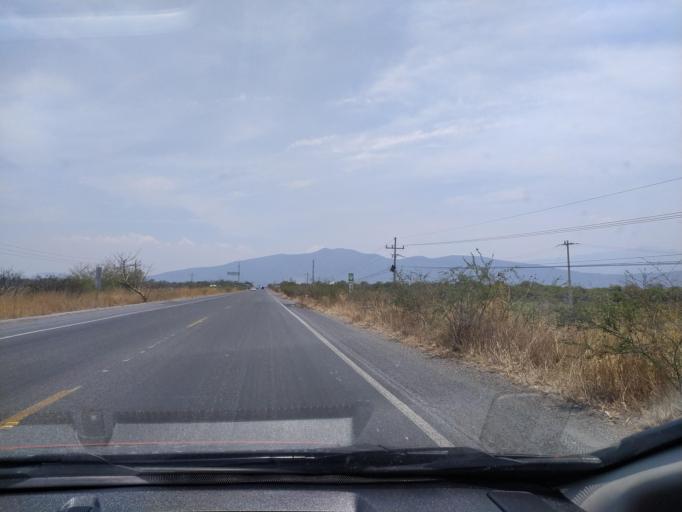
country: MX
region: Jalisco
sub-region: Zacoalco de Torres
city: Barranca de Otates (Barranca de Otatan)
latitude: 20.3029
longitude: -103.5976
